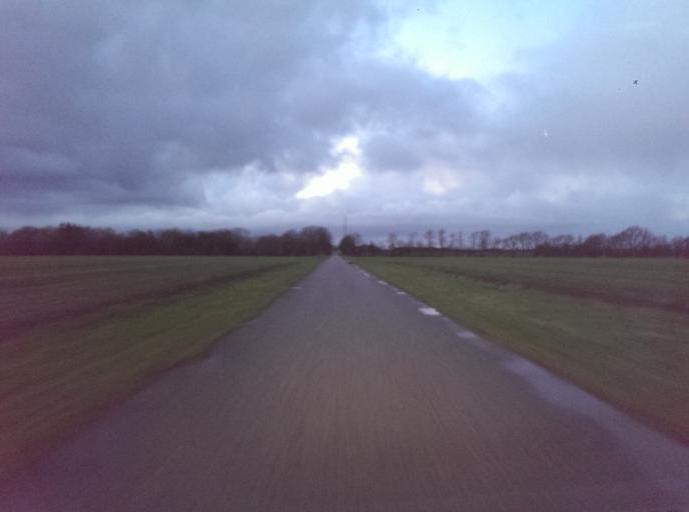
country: DK
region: South Denmark
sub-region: Esbjerg Kommune
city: Bramming
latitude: 55.4318
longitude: 8.6672
